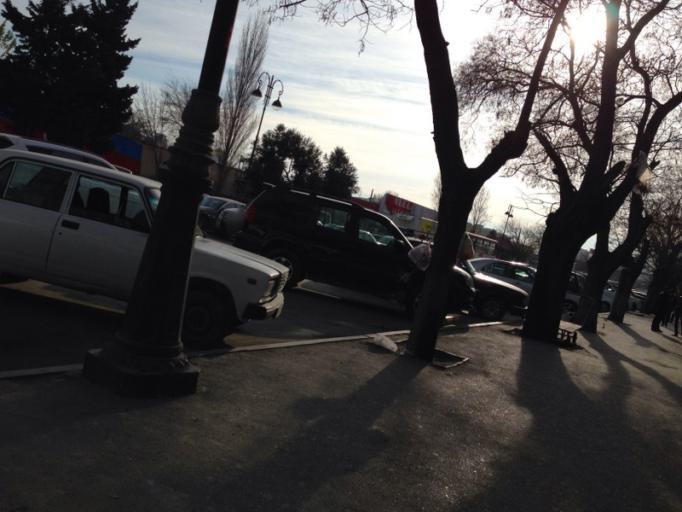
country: AZ
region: Baki
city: Baku
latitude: 40.3894
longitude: 49.8595
